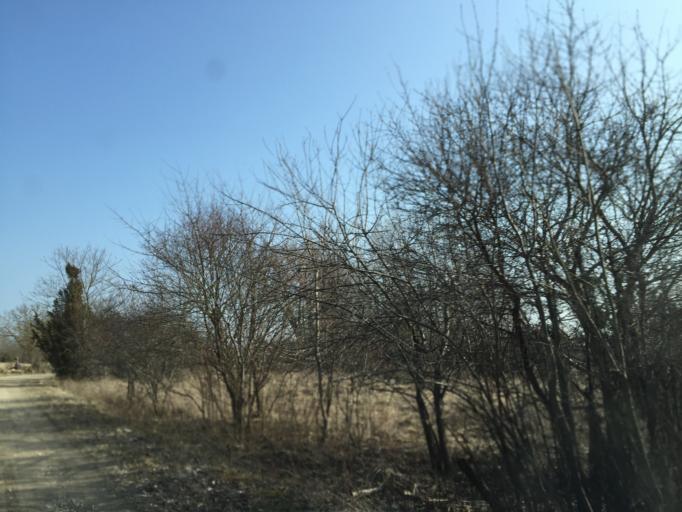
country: EE
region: Saare
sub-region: Orissaare vald
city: Orissaare
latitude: 58.4813
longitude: 23.1163
